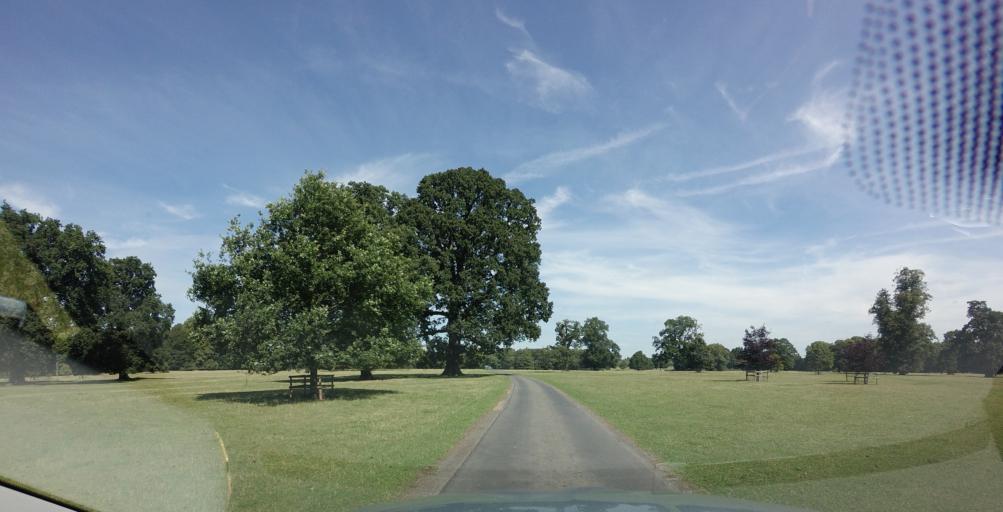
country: GB
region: England
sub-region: North Yorkshire
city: Ripon
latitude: 54.1037
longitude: -1.4667
